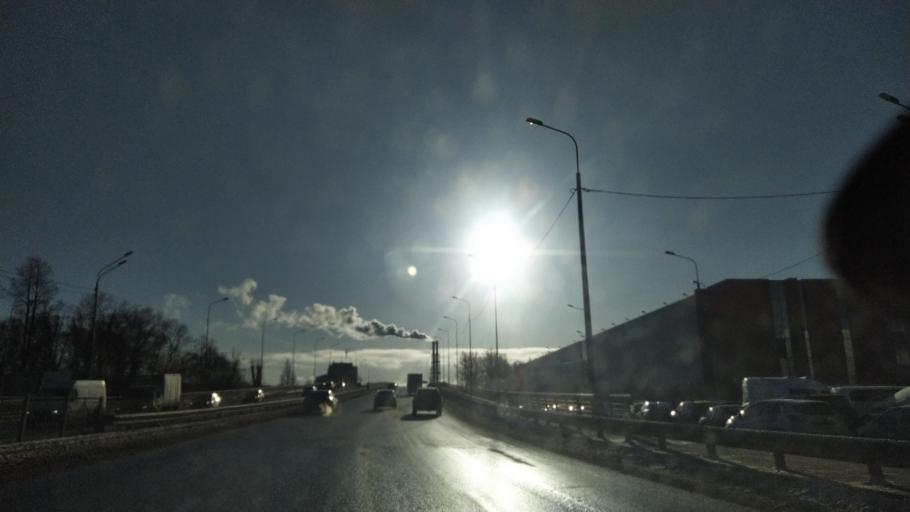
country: RU
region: Leningrad
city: Chernaya Rechka
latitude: 59.9959
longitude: 30.3001
